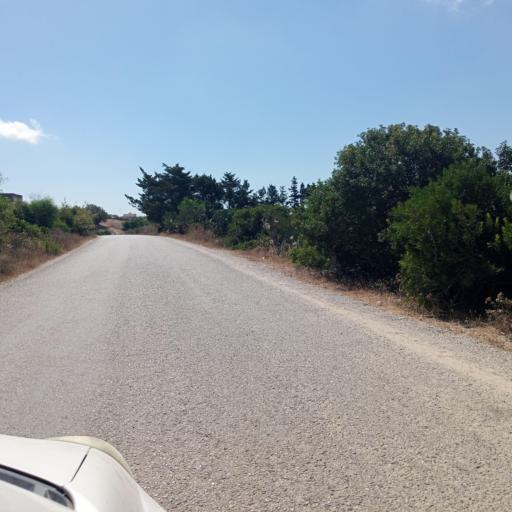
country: TN
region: Nabul
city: Qulaybiyah
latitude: 36.8605
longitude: 11.0434
